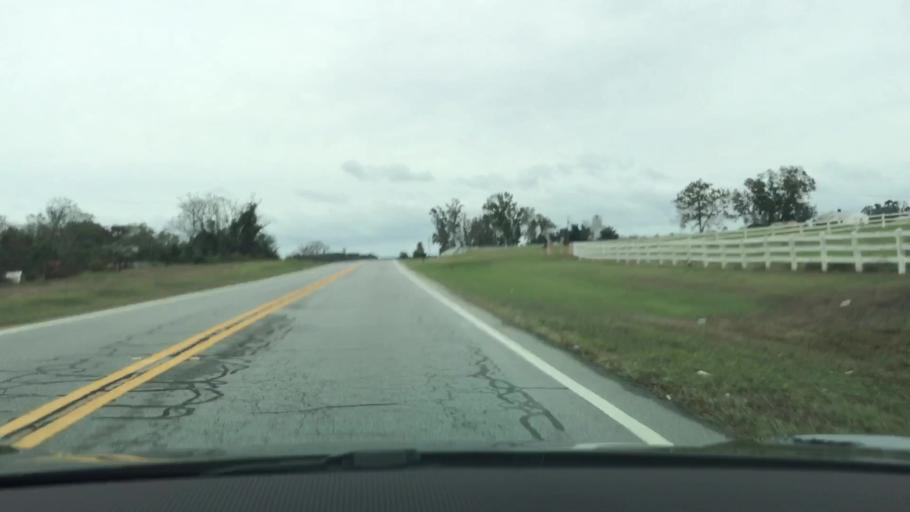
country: US
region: Georgia
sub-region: Warren County
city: Warrenton
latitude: 33.3729
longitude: -82.6024
